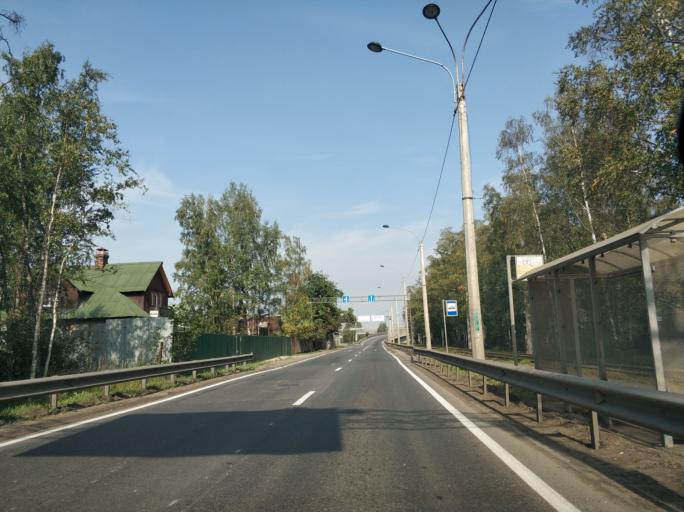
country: RU
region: St.-Petersburg
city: Krasnogvargeisky
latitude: 59.9771
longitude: 30.5059
